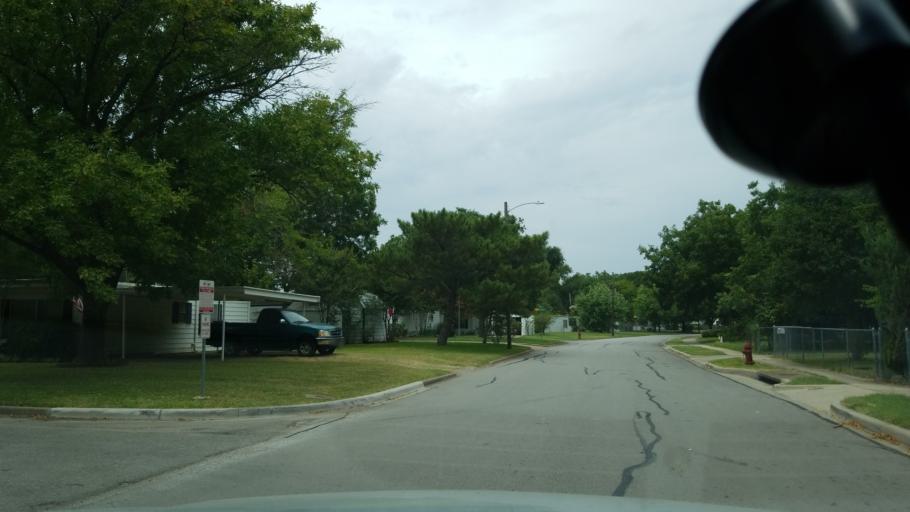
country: US
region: Texas
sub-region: Dallas County
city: Grand Prairie
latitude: 32.7397
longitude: -96.9915
